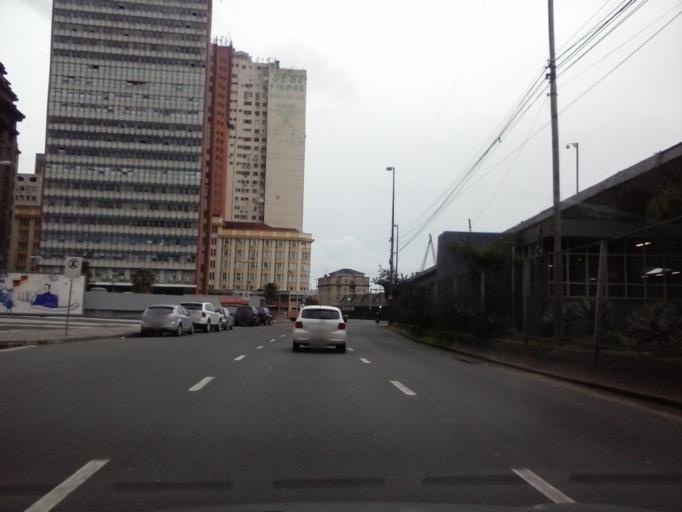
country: BR
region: Rio Grande do Sul
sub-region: Porto Alegre
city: Porto Alegre
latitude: -30.0263
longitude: -51.2276
